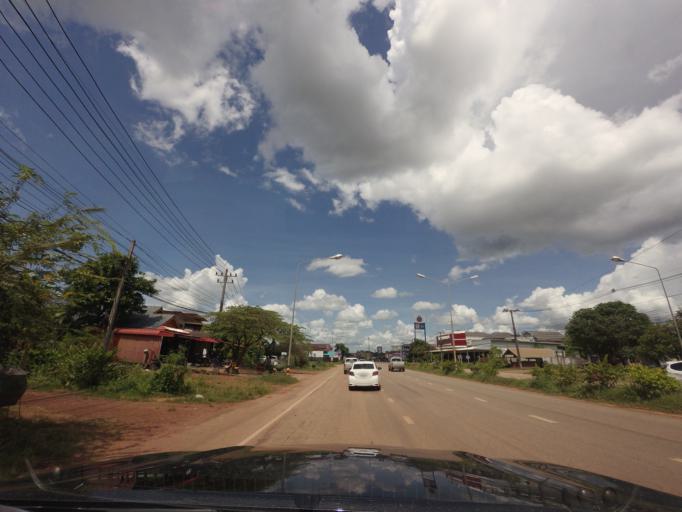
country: TH
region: Changwat Udon Thani
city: Ban Dung
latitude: 17.6768
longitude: 103.2532
